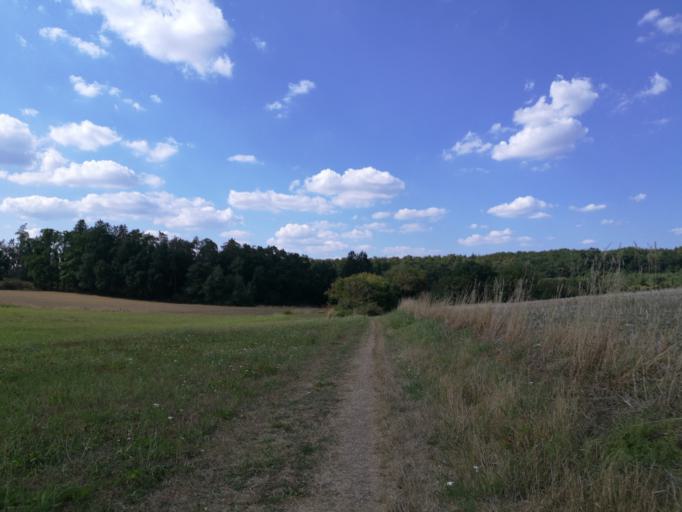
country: DE
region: Bavaria
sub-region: Regierungsbezirk Mittelfranken
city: Seukendorf
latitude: 49.4825
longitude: 10.9076
